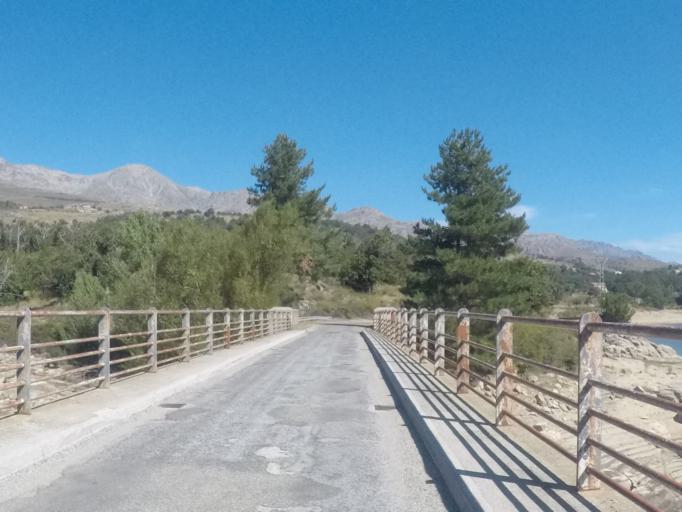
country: FR
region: Corsica
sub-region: Departement de la Haute-Corse
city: Corte
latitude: 42.3236
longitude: 8.9969
